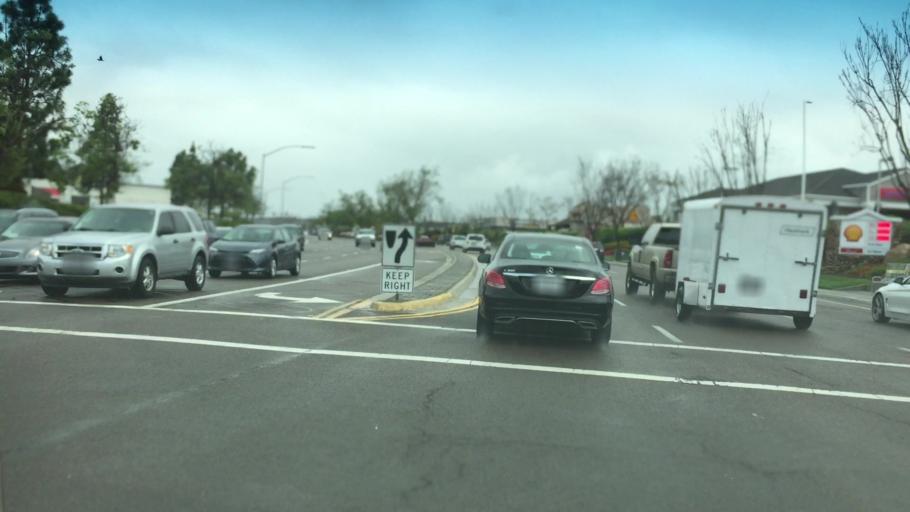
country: US
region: California
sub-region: San Diego County
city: Poway
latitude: 32.9804
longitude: -117.0781
